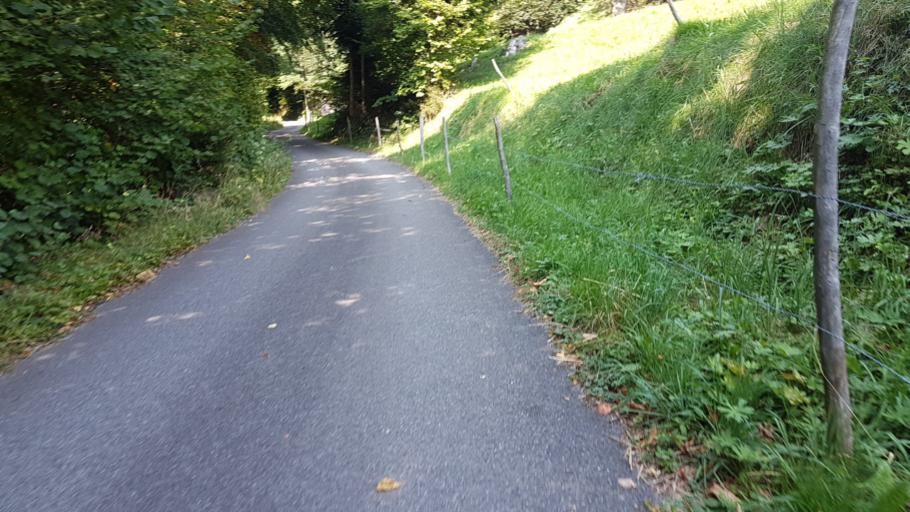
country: CH
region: Bern
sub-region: Frutigen-Niedersimmental District
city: Aeschi
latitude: 46.5973
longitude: 7.7167
